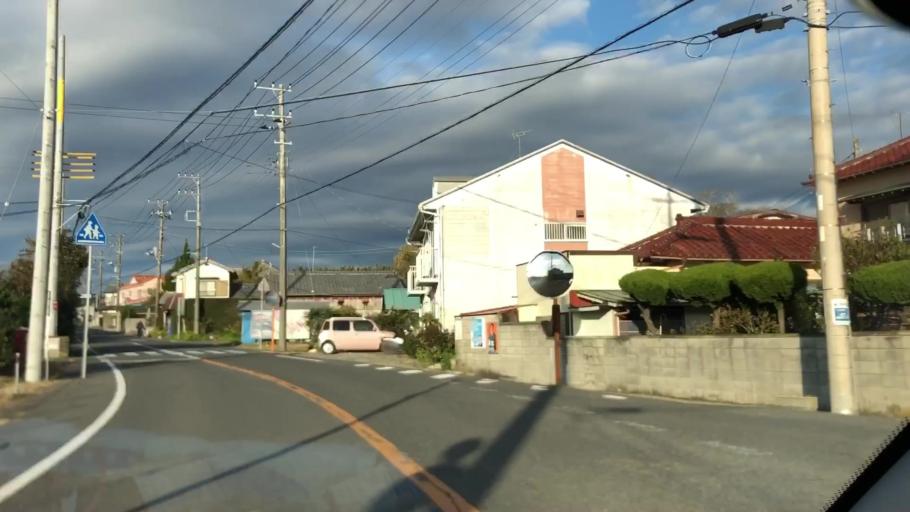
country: JP
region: Chiba
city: Tateyama
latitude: 34.9756
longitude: 139.9573
